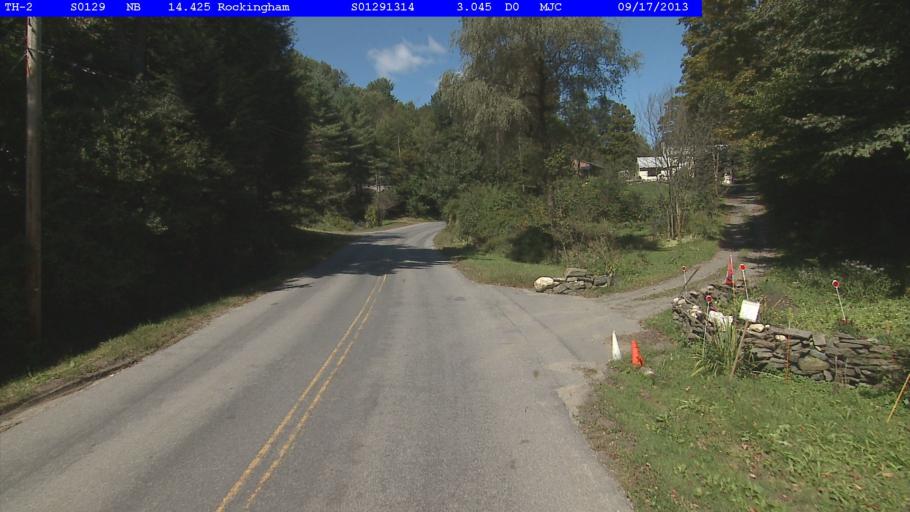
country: US
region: Vermont
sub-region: Windham County
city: Rockingham
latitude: 43.1612
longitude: -72.5175
